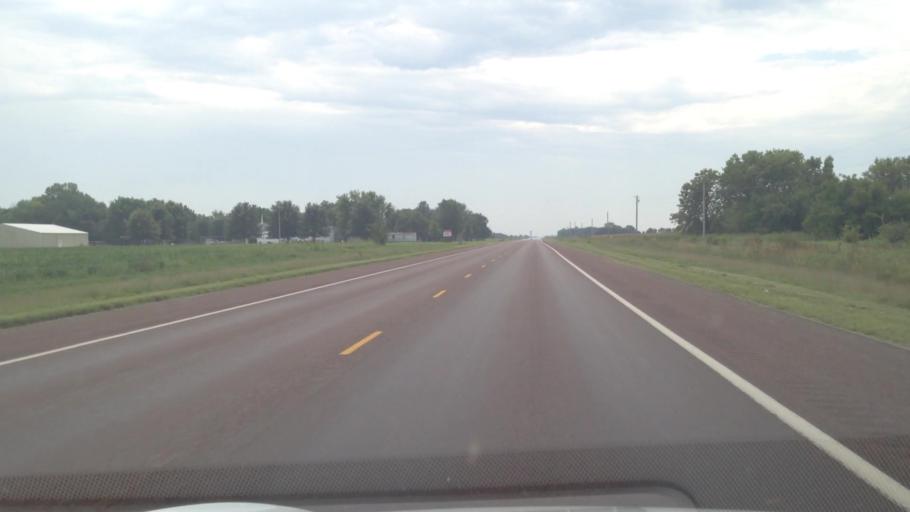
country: US
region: Kansas
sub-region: Crawford County
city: Girard
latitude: 37.4424
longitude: -94.8330
